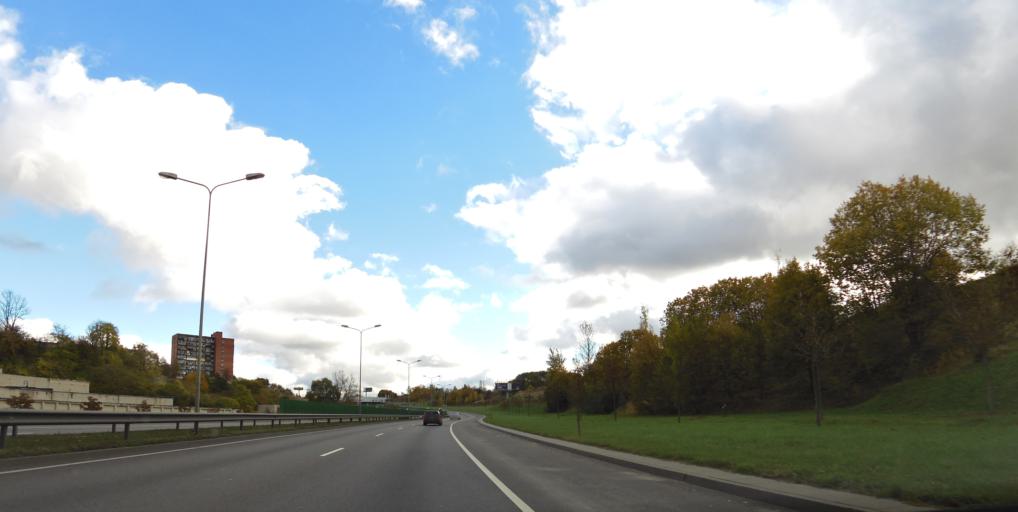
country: LT
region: Vilnius County
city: Vilkpede
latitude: 54.6597
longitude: 25.2634
